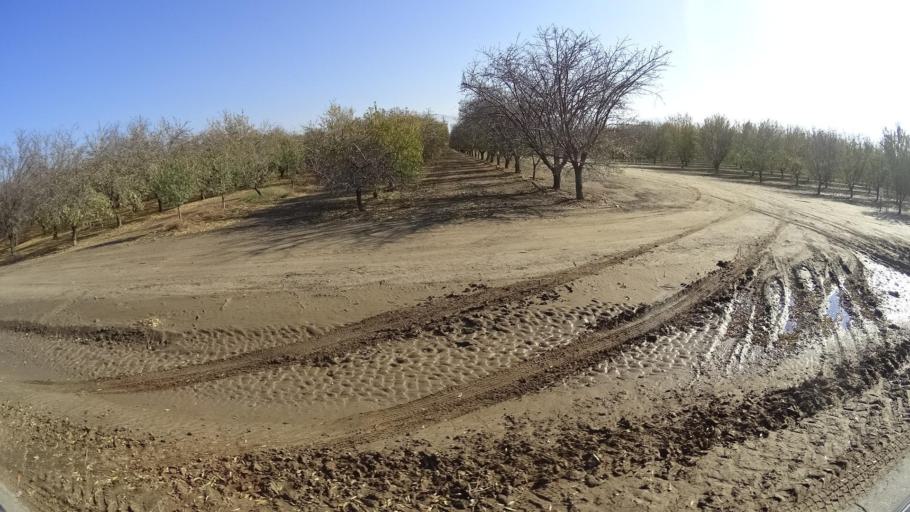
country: US
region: California
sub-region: Kern County
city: Arvin
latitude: 35.1870
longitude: -118.8781
